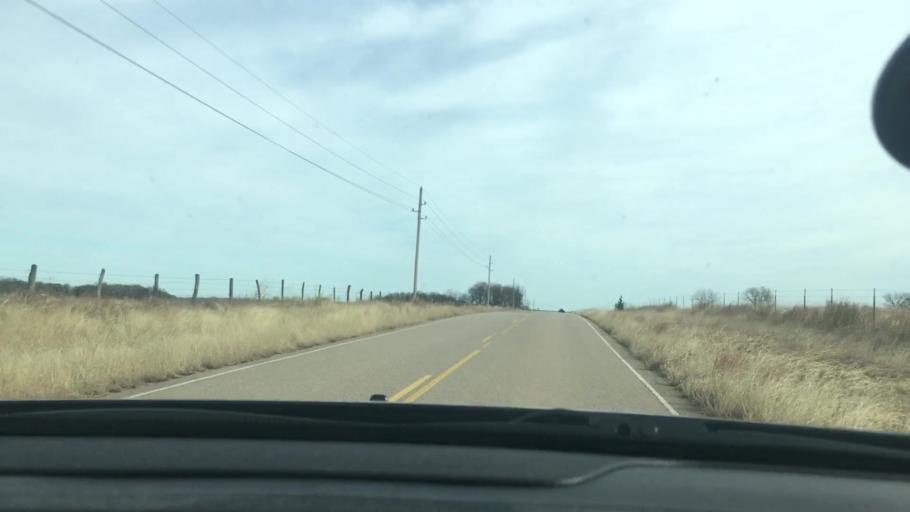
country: US
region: Oklahoma
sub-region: Murray County
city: Sulphur
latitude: 34.4049
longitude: -96.8932
